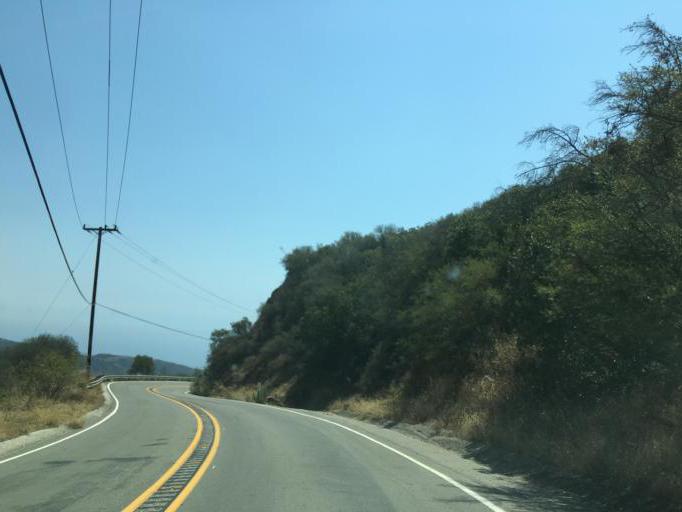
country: US
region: California
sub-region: Los Angeles County
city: Las Flores
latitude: 34.0741
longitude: -118.6521
